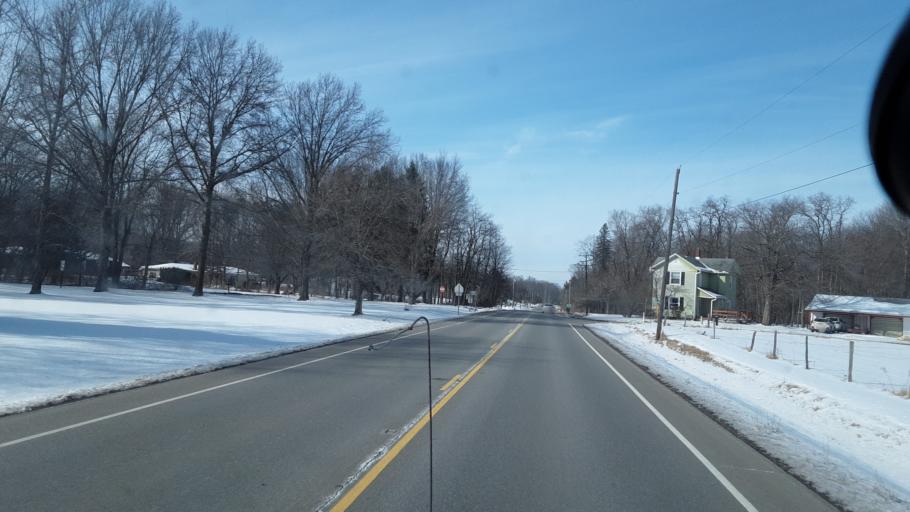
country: US
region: Ohio
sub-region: Mahoning County
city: Canfield
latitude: 40.9584
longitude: -80.7441
